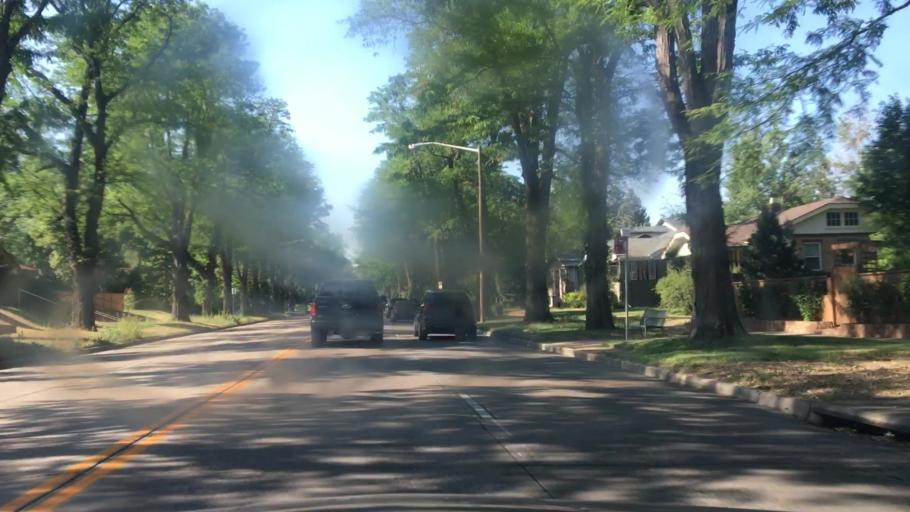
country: US
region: Colorado
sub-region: Arapahoe County
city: Glendale
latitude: 39.7000
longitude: -104.9593
